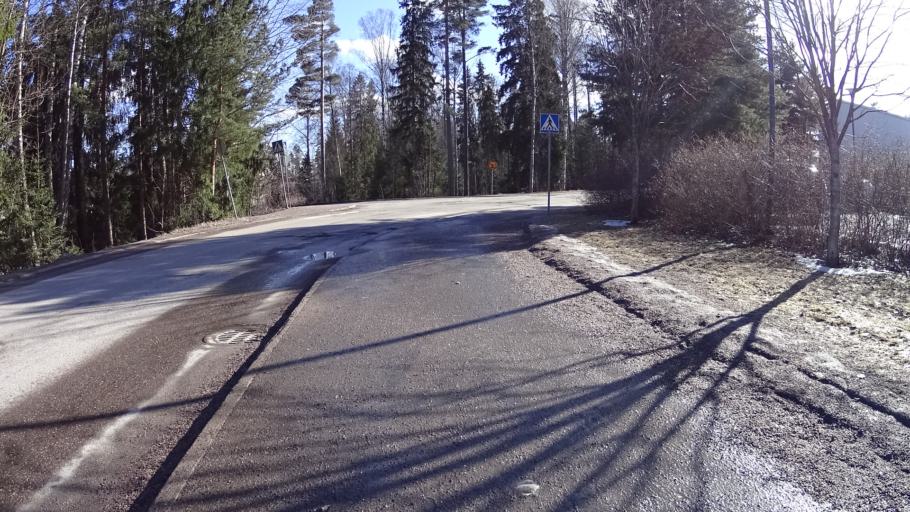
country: FI
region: Uusimaa
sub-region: Helsinki
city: Kilo
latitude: 60.2460
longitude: 24.7698
